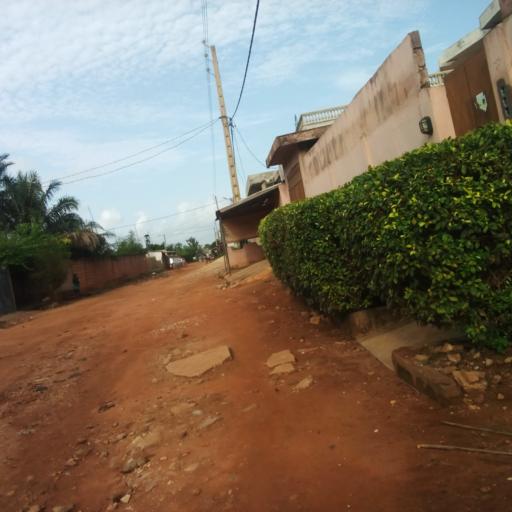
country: BJ
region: Atlantique
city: Abomey-Calavi
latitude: 6.4361
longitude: 2.3432
